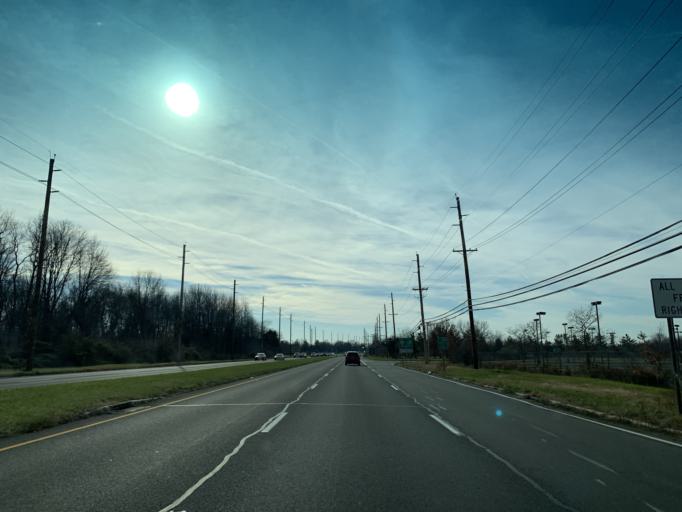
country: US
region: New Jersey
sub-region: Middlesex County
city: Dayton
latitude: 40.3497
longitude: -74.4970
